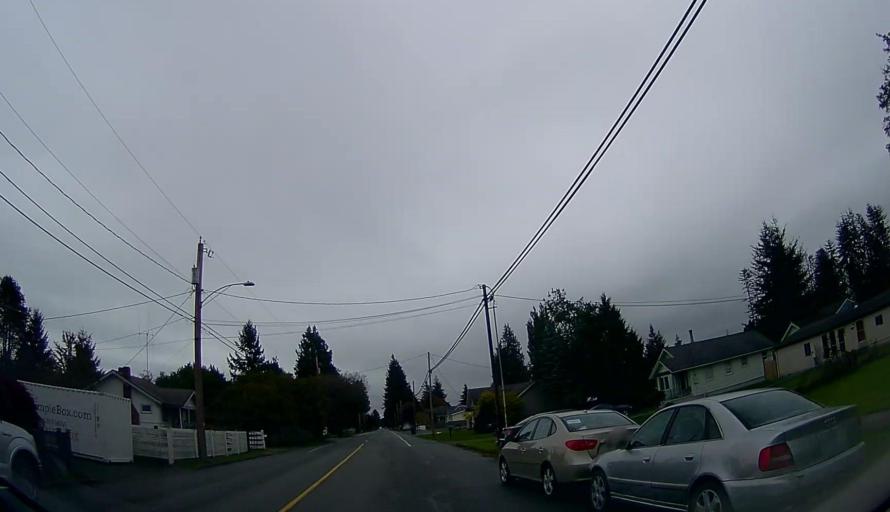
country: US
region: Washington
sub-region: Skagit County
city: Sedro-Woolley
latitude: 48.5032
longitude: -122.2203
